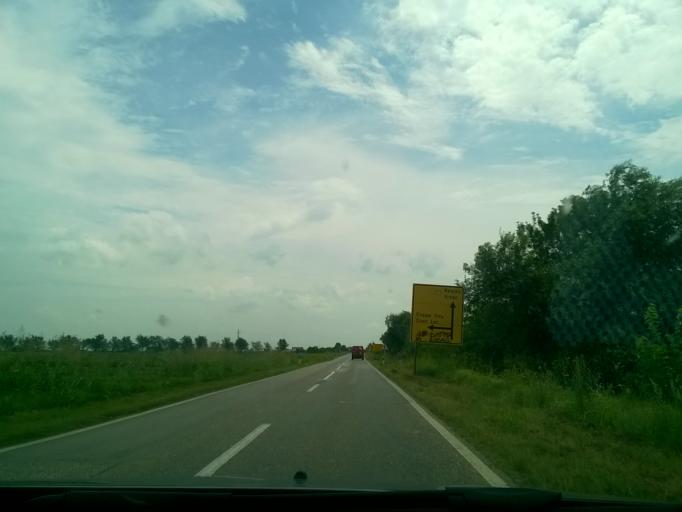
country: RS
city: Stari Lec
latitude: 45.2757
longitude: 20.9446
